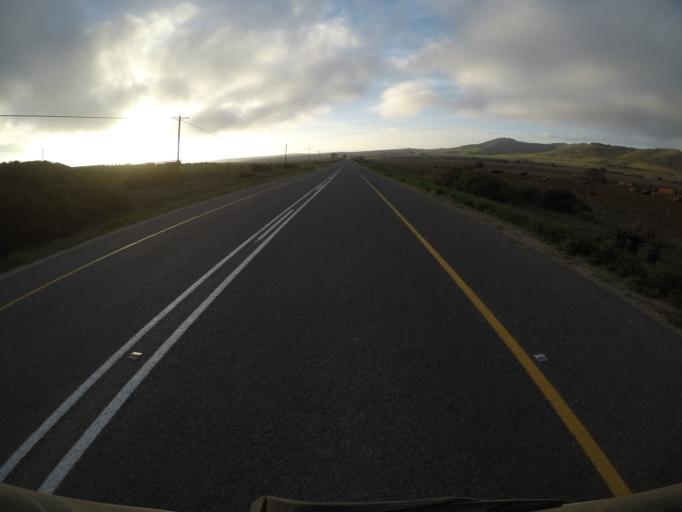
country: ZA
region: Western Cape
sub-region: Eden District Municipality
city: Mossel Bay
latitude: -34.1103
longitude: 22.0747
